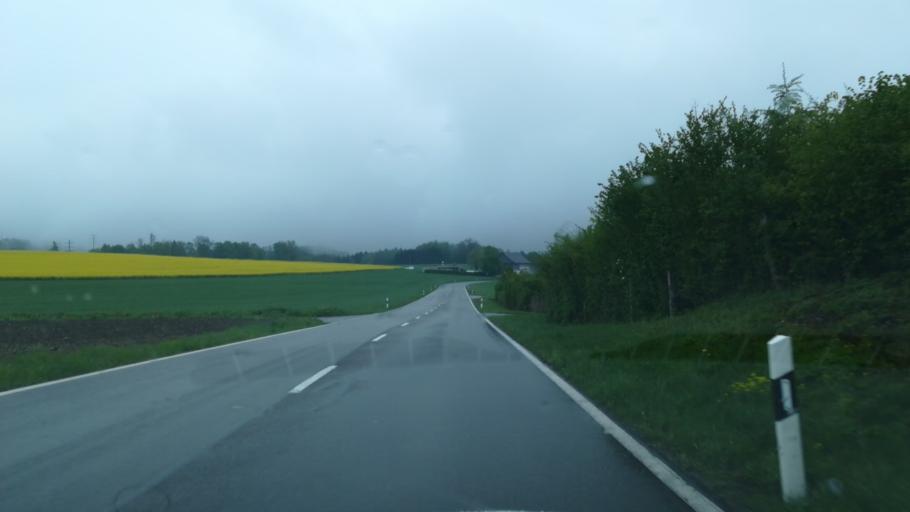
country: CH
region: Zurich
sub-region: Bezirk Winterthur
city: Brutten
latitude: 47.4678
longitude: 8.6822
